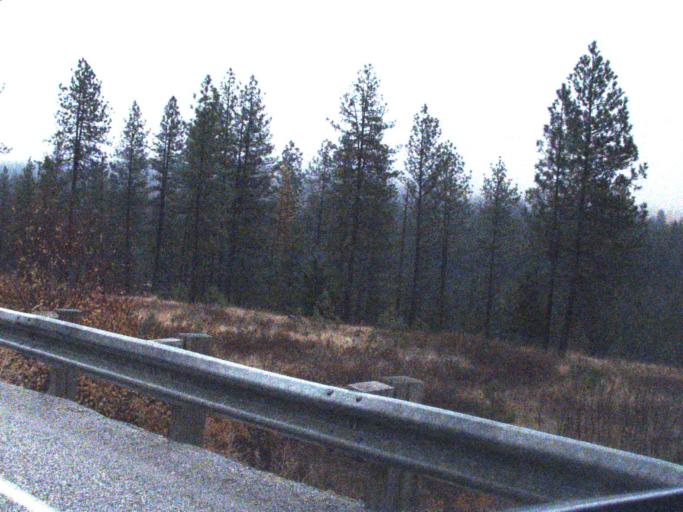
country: US
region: Washington
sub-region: Stevens County
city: Kettle Falls
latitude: 48.7541
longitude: -118.1345
